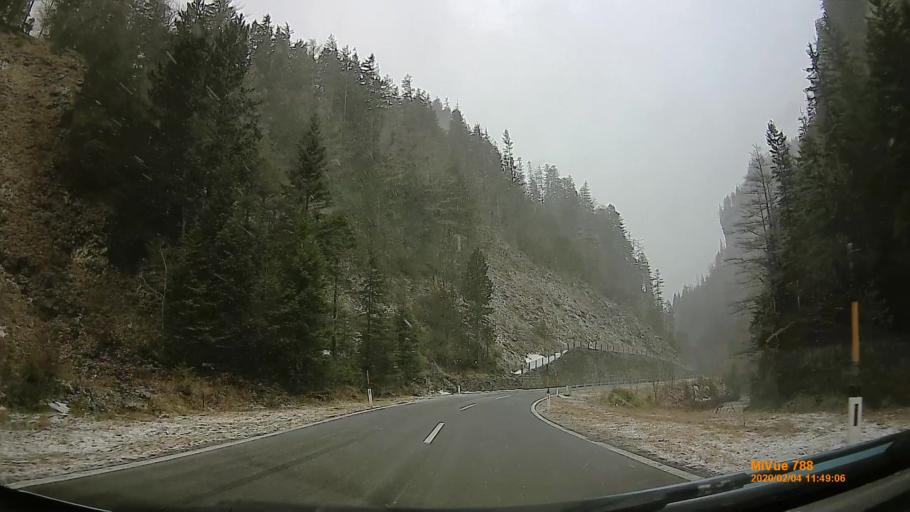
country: AT
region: Styria
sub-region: Politischer Bezirk Bruck-Muerzzuschlag
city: Muerzsteg
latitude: 47.7220
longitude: 15.4838
